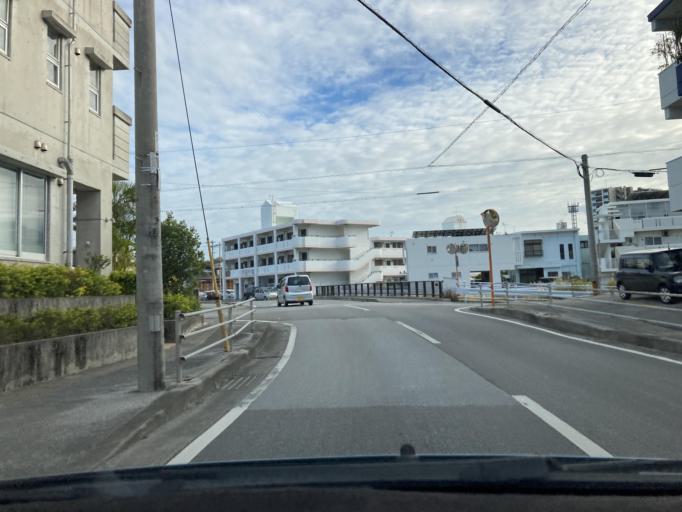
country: JP
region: Okinawa
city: Tomigusuku
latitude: 26.1993
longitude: 127.7321
